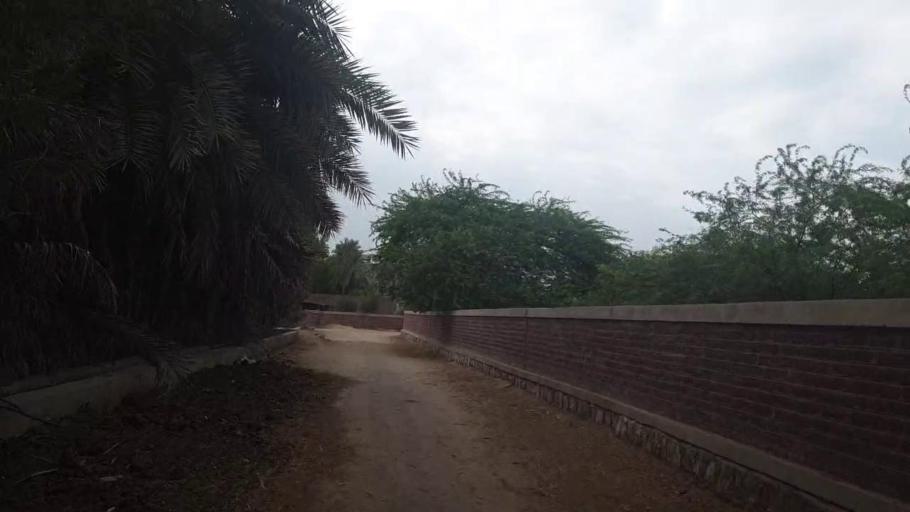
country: PK
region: Sindh
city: Sukkur
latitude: 27.6360
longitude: 68.7930
